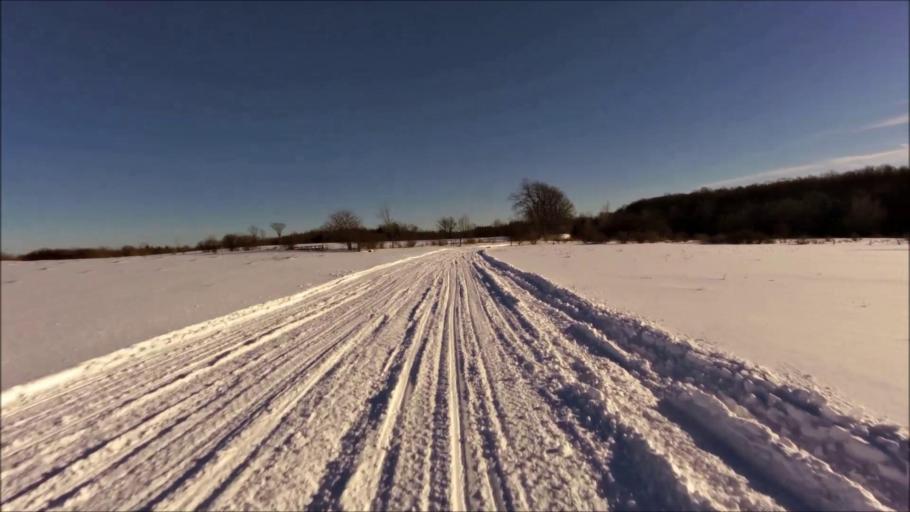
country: US
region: New York
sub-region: Chautauqua County
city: Mayville
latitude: 42.2589
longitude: -79.3871
